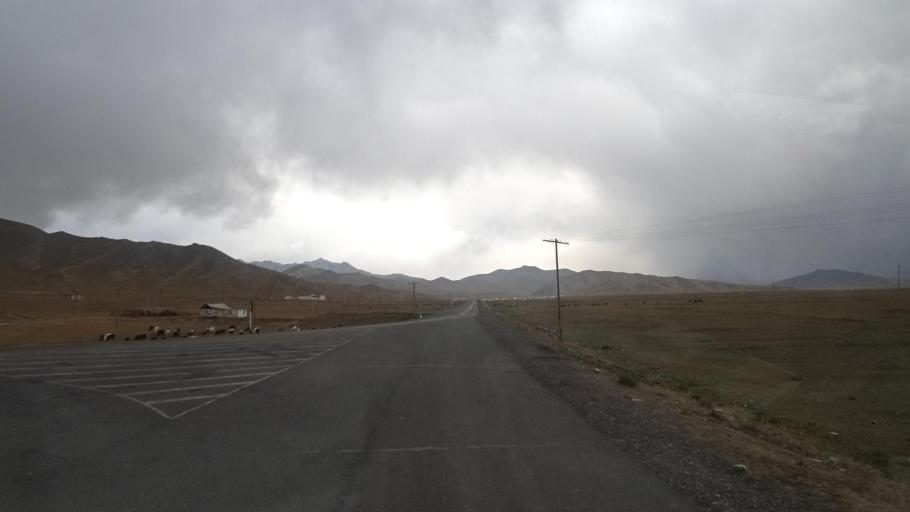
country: KG
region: Osh
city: Gul'cha
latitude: 39.7057
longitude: 73.2293
